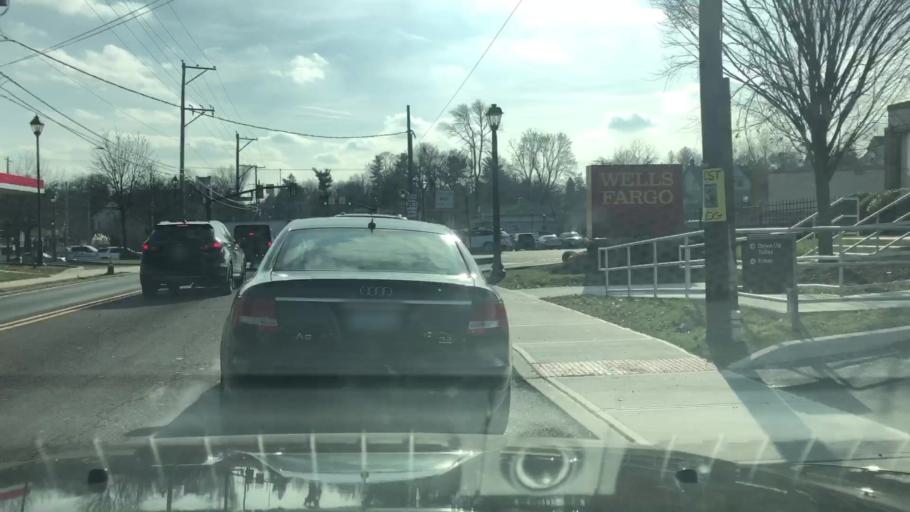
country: US
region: Pennsylvania
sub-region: Bucks County
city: Langhorne
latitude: 40.1776
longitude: -74.9177
